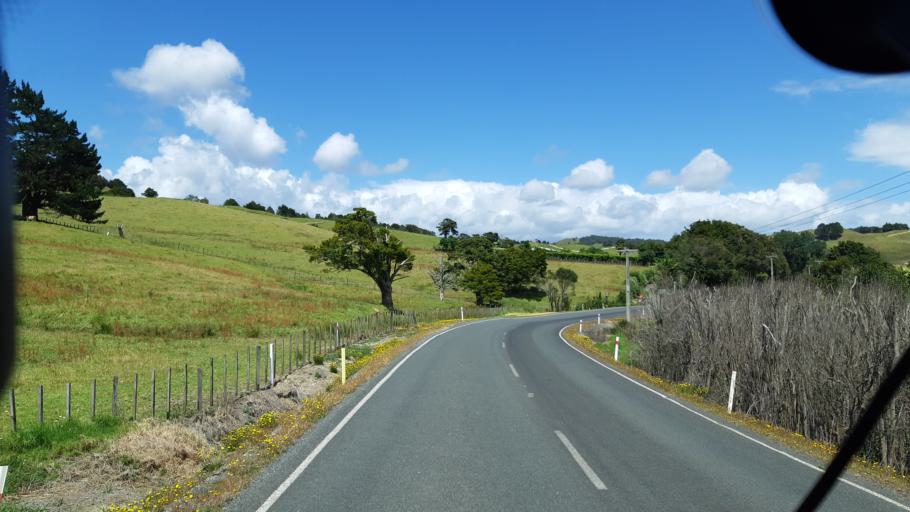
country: NZ
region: Northland
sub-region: Far North District
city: Taipa
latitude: -35.2688
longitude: 173.4949
